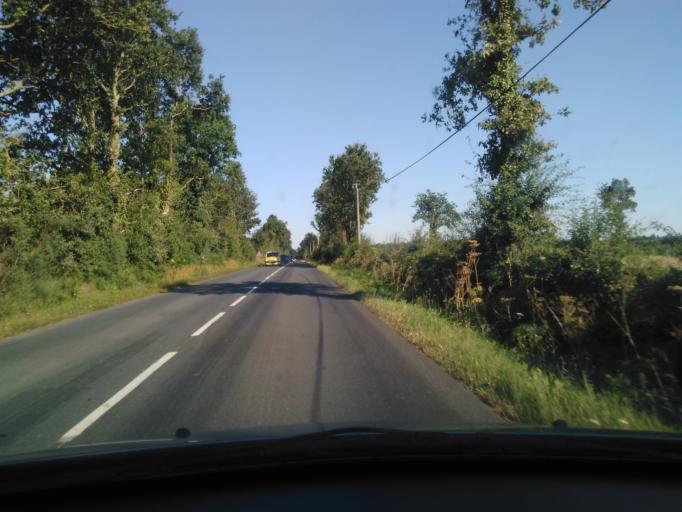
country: FR
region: Pays de la Loire
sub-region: Departement de la Vendee
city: Dompierre-sur-Yon
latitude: 46.7305
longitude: -1.3652
